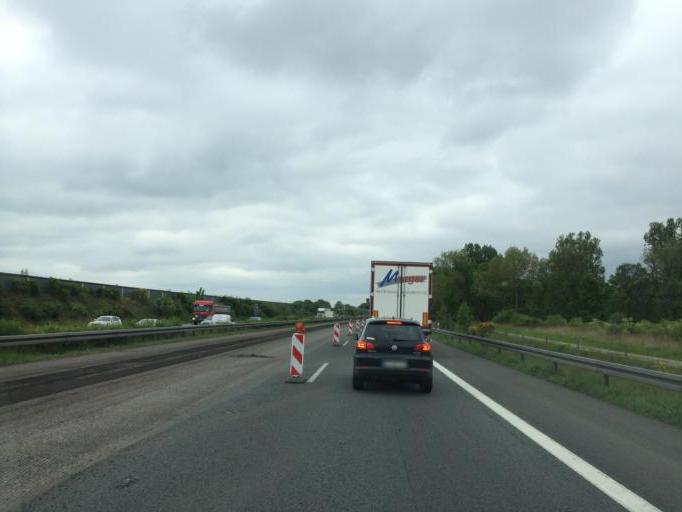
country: DE
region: Lower Saxony
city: Klein Schwulper
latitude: 52.3296
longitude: 10.4527
